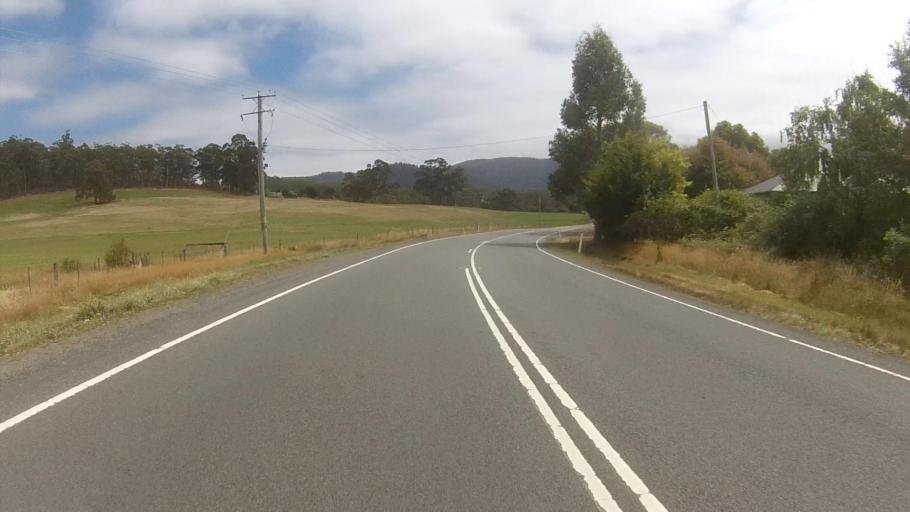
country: AU
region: Tasmania
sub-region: Kingborough
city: Margate
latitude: -42.9920
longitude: 147.1988
